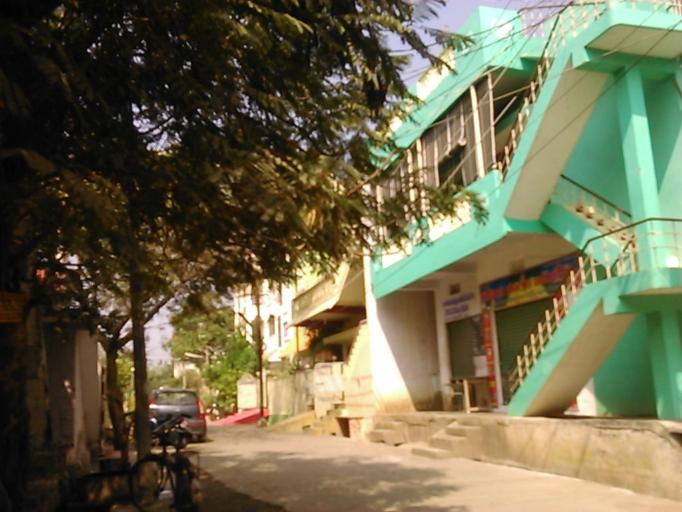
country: IN
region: Andhra Pradesh
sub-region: Guntur
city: Bhattiprolu
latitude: 16.2384
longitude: 80.6557
